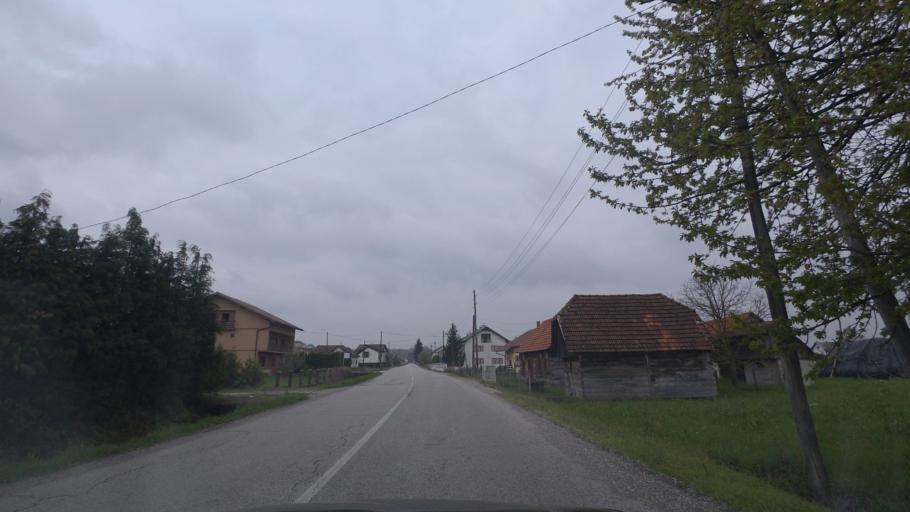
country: HR
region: Zagrebacka
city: Jastrebarsko
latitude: 45.6128
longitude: 15.5923
